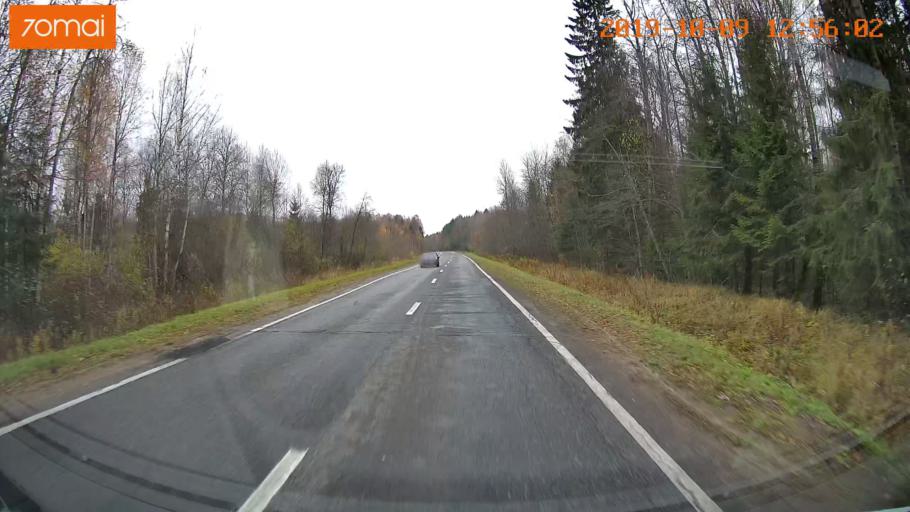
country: RU
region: Jaroslavl
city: Prechistoye
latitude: 58.3962
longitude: 40.4081
